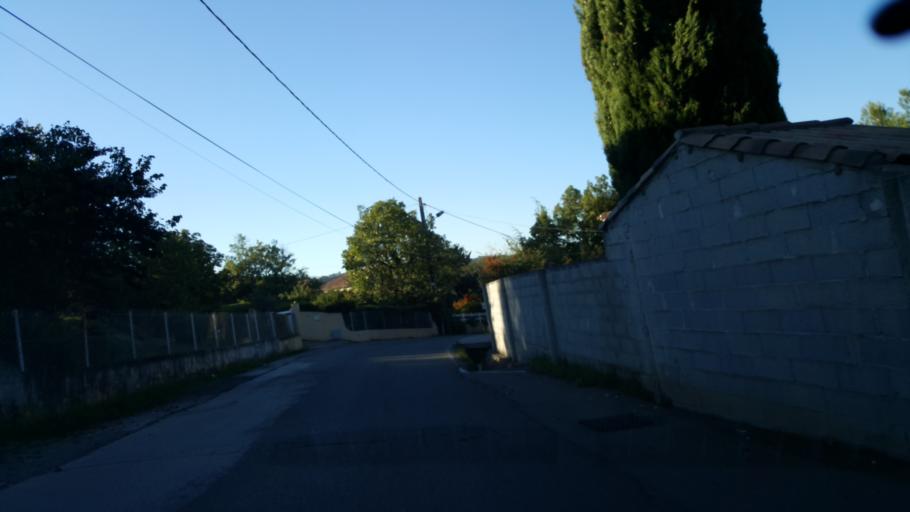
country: FR
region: Provence-Alpes-Cote d'Azur
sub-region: Departement du Var
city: Saint-Maximin-la-Sainte-Baume
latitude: 43.4523
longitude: 5.8507
